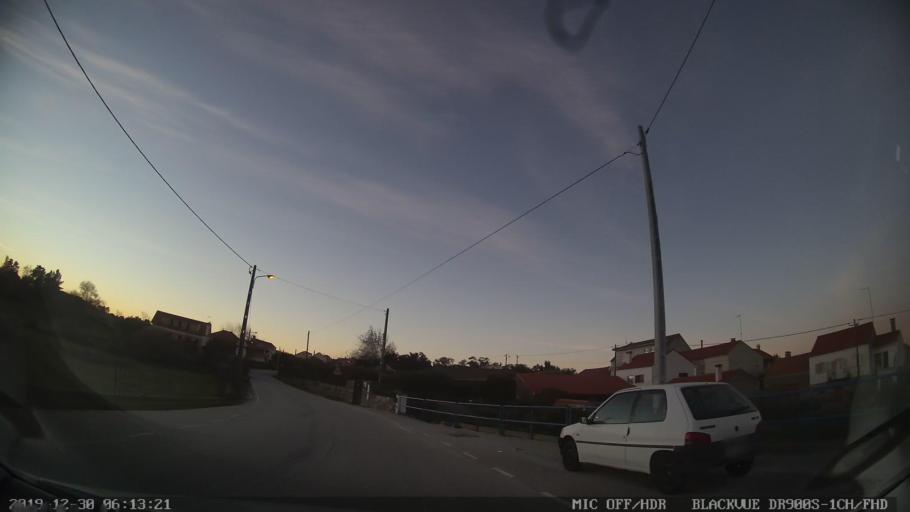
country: PT
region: Castelo Branco
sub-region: Penamacor
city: Penamacor
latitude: 40.1116
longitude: -7.2100
